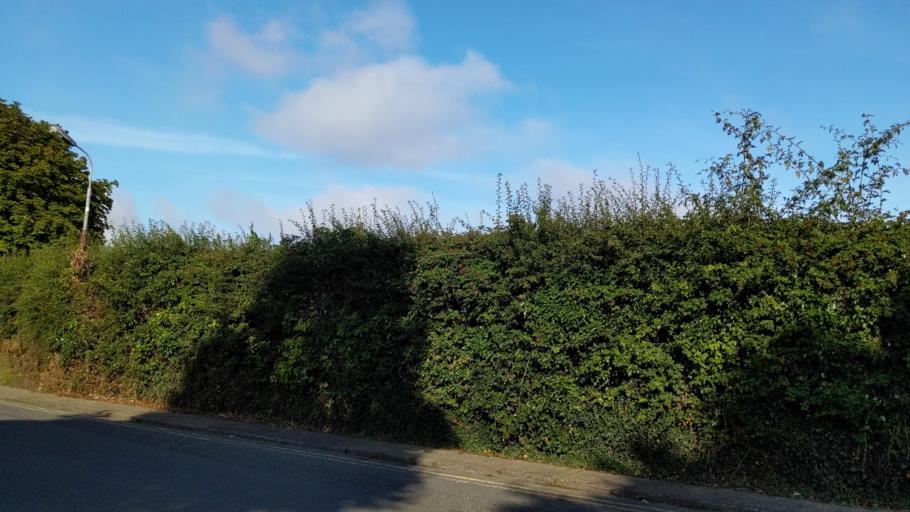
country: IE
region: Leinster
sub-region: Lu
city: Drogheda
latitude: 53.7075
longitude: -6.3426
